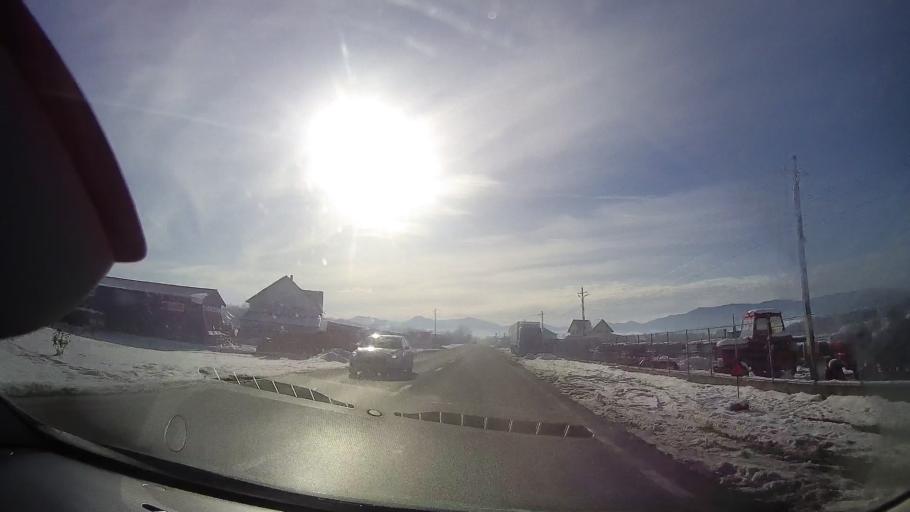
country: RO
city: Vanatori-Neamt
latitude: 47.1711
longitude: 26.3233
